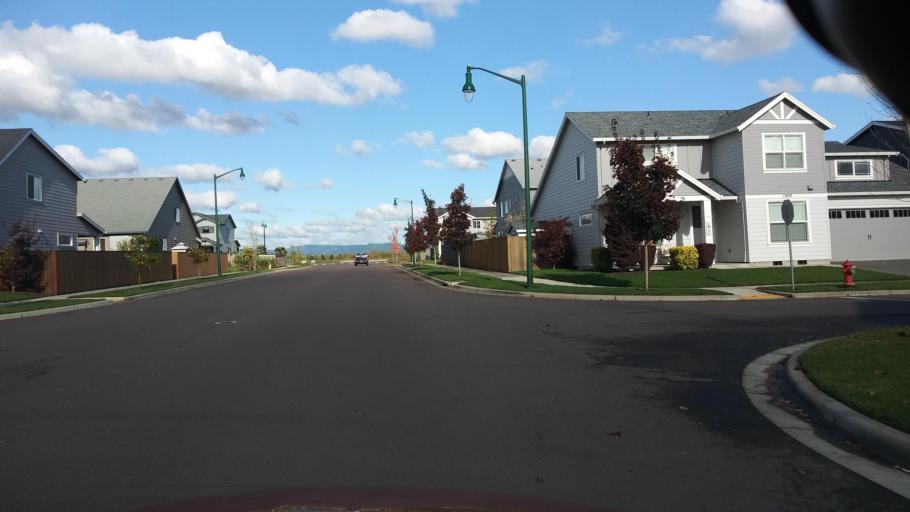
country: US
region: Oregon
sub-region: Washington County
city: Forest Grove
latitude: 45.5379
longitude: -123.1170
